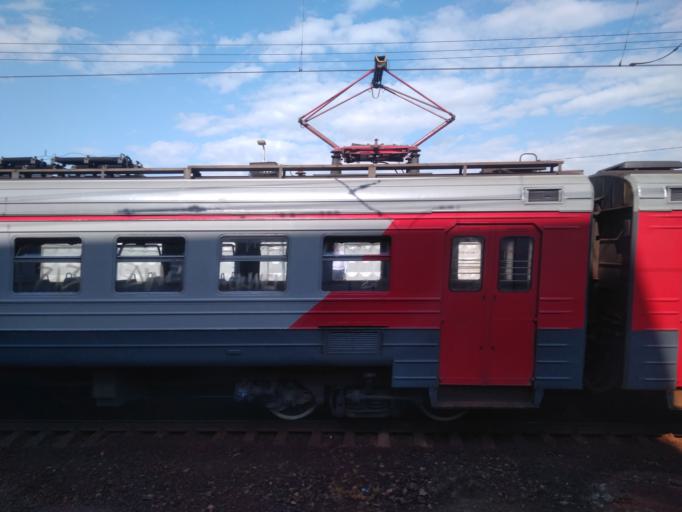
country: RU
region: Moscow
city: Sokol'niki
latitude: 55.7776
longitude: 37.6505
